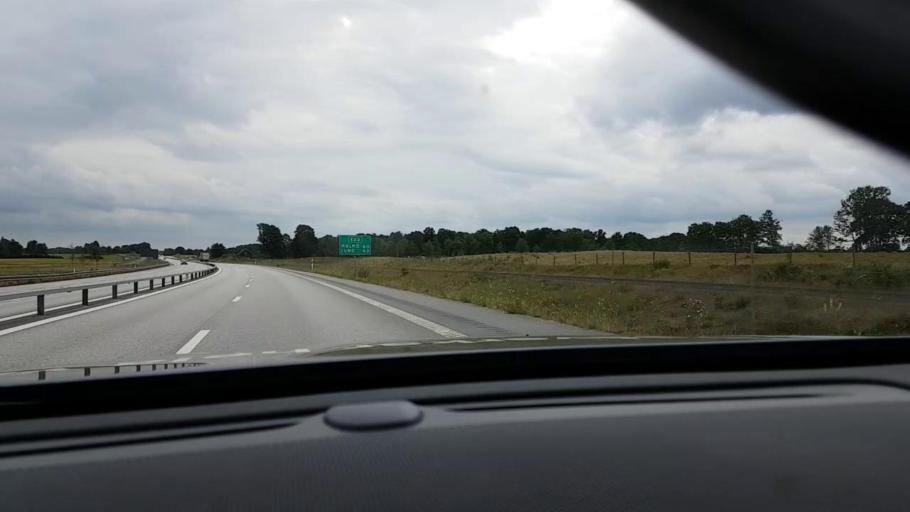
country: SE
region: Skane
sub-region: Horby Kommun
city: Hoerby
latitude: 55.8990
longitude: 13.7254
